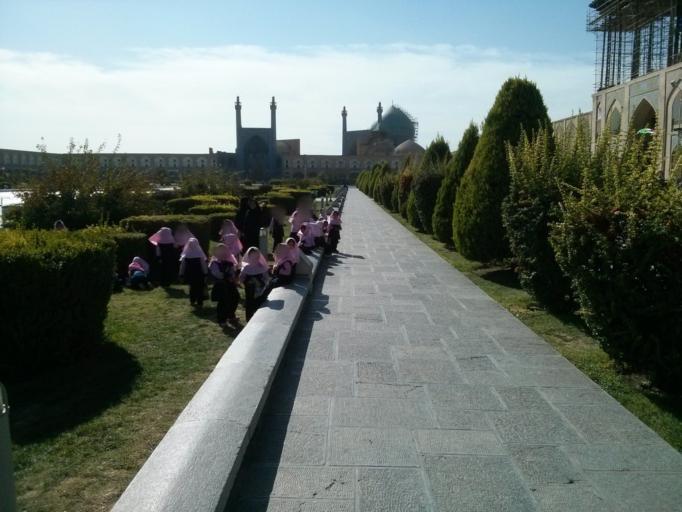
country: IR
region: Isfahan
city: Kashan
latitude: 34.0063
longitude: 51.4090
